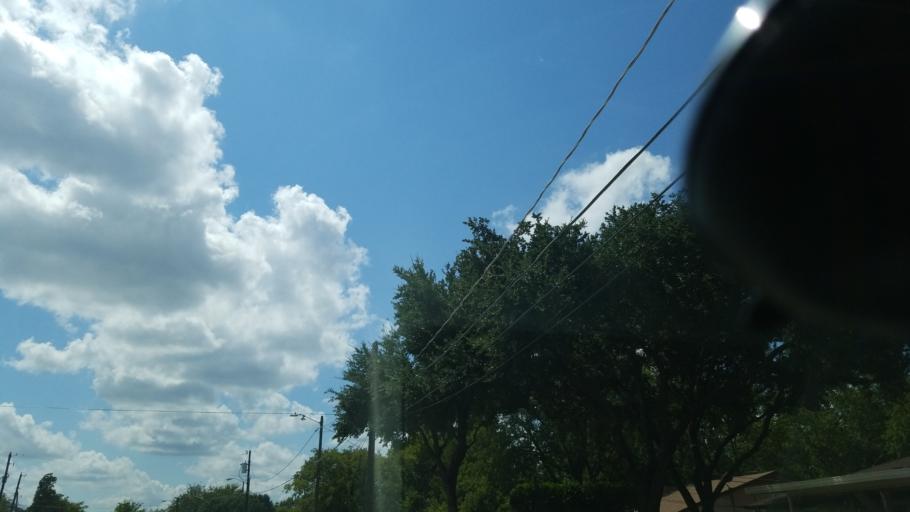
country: US
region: Texas
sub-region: Dallas County
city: Grand Prairie
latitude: 32.7128
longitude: -96.9861
